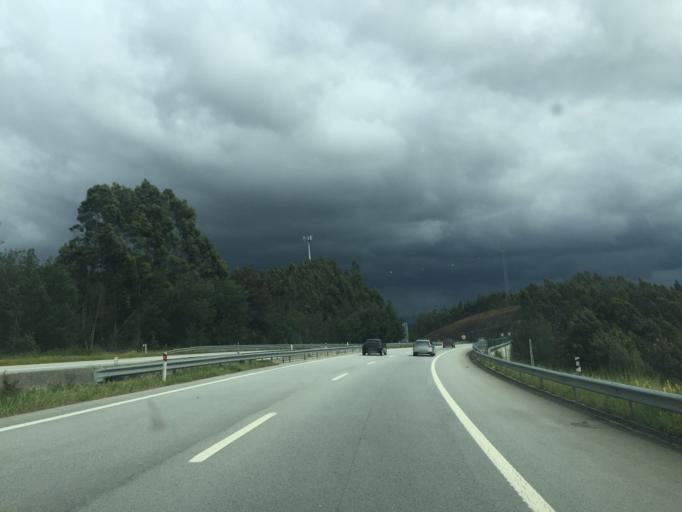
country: PT
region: Aveiro
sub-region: Albergaria-A-Velha
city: Albergaria-a-Velha
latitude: 40.6779
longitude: -8.4614
